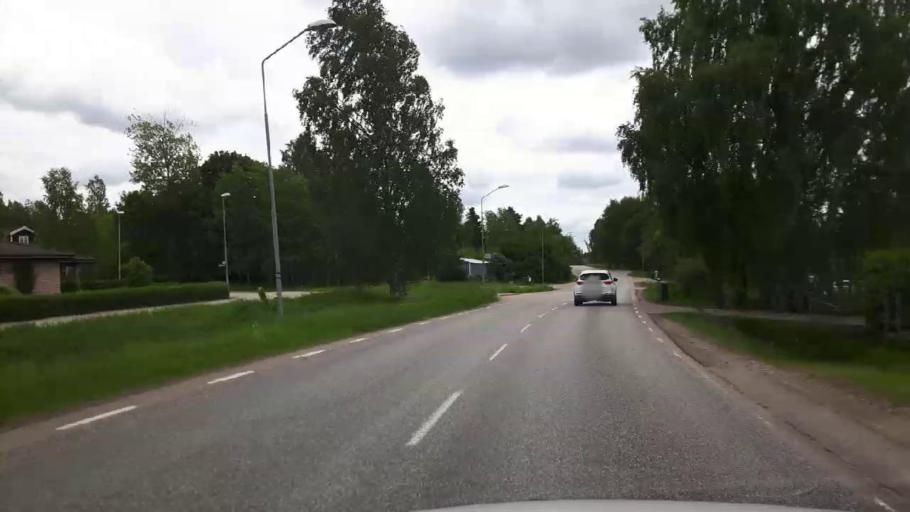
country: SE
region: Vaestmanland
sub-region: Norbergs Kommun
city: Norberg
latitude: 60.1003
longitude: 15.9289
